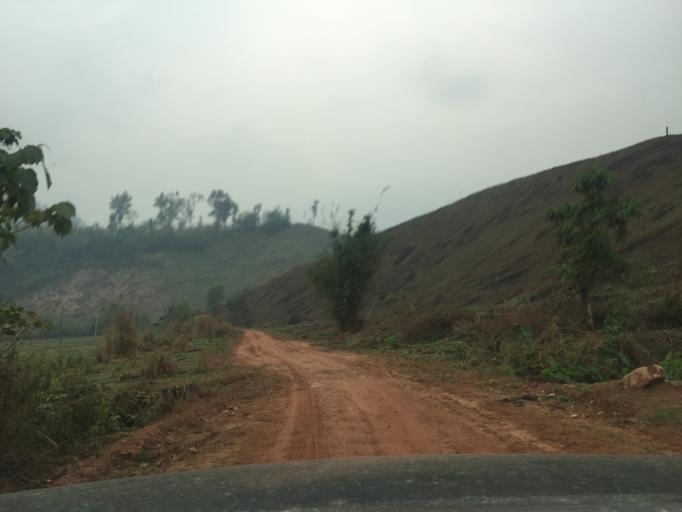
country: TH
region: Nan
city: Bo Kluea
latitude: 18.8485
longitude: 101.4174
